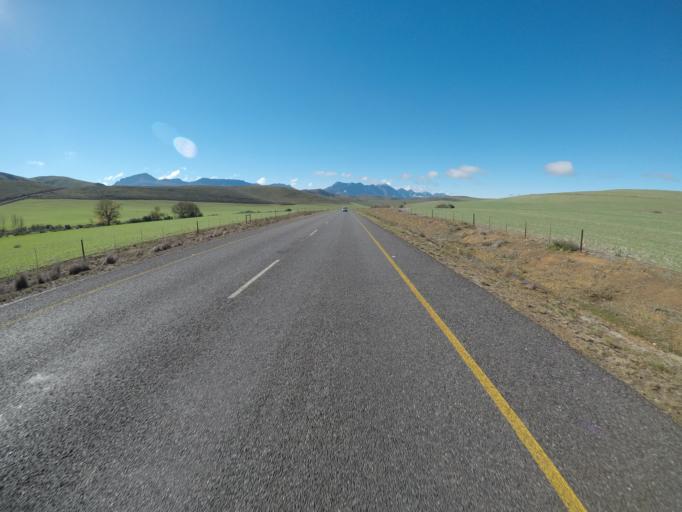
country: ZA
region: Western Cape
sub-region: Overberg District Municipality
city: Caledon
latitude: -34.0962
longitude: 19.5371
